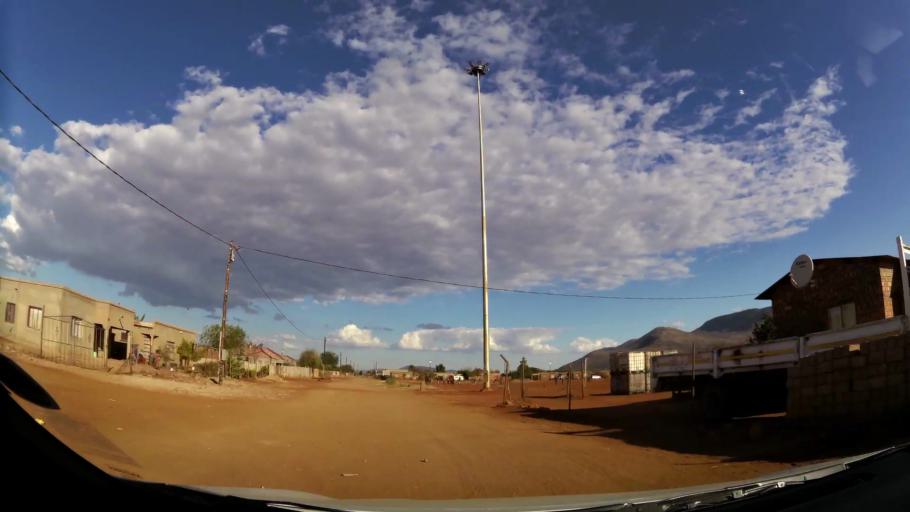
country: ZA
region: Limpopo
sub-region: Waterberg District Municipality
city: Mokopane
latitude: -24.1827
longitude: 28.9711
